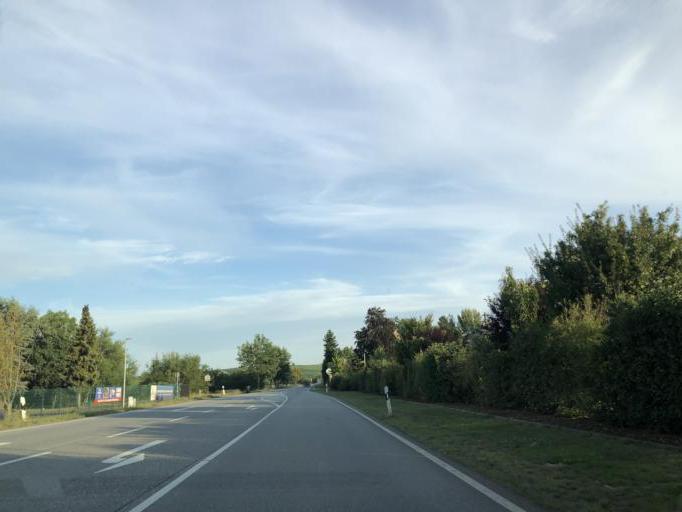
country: DE
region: Rheinland-Pfalz
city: Grolsheim
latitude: 49.8910
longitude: 7.9204
